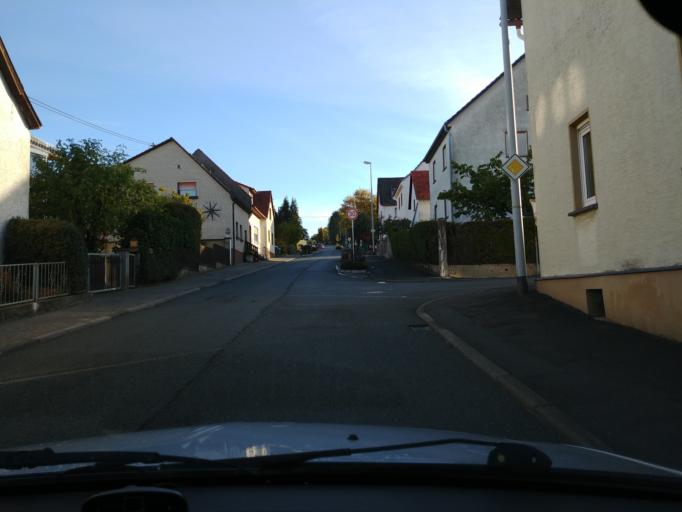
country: DE
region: Hesse
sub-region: Regierungsbezirk Darmstadt
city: Waldems
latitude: 50.2742
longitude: 8.3464
